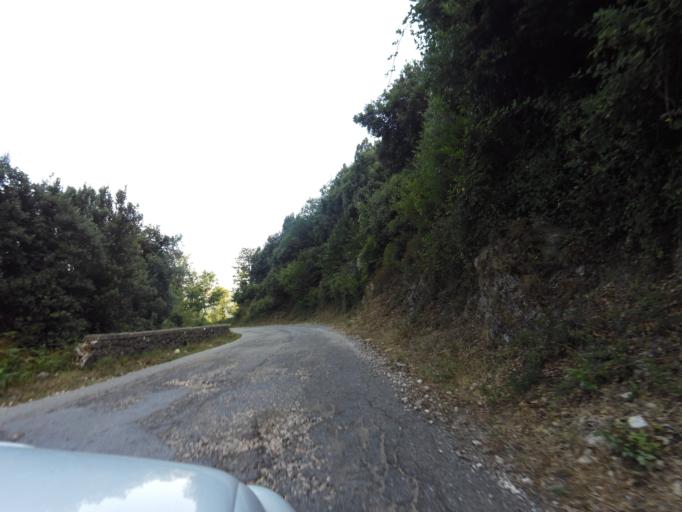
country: IT
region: Calabria
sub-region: Provincia di Reggio Calabria
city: Pazzano
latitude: 38.4723
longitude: 16.4076
